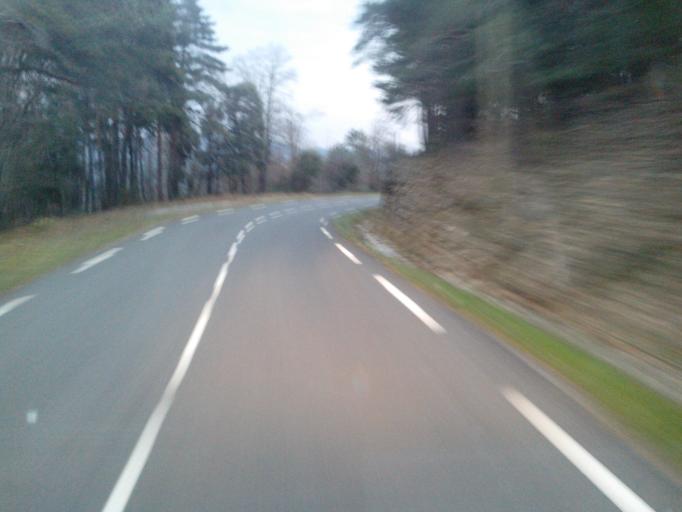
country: FR
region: Languedoc-Roussillon
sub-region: Departement du Gard
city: Valleraugue
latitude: 44.1570
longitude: 3.7487
